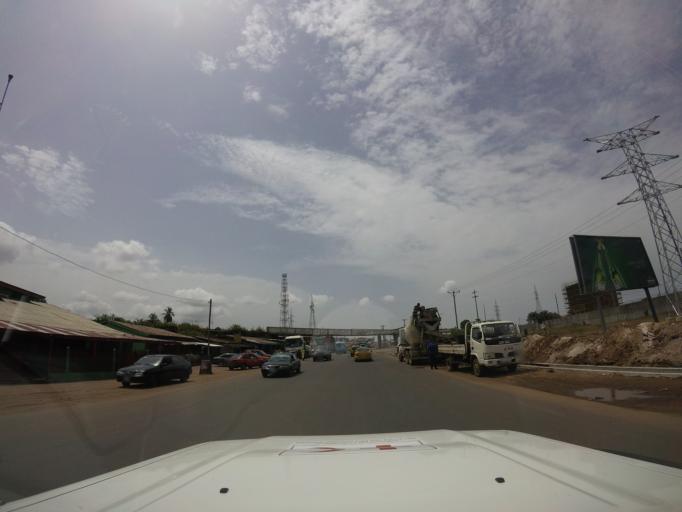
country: LR
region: Montserrado
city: Monrovia
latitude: 6.3612
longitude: -10.7865
